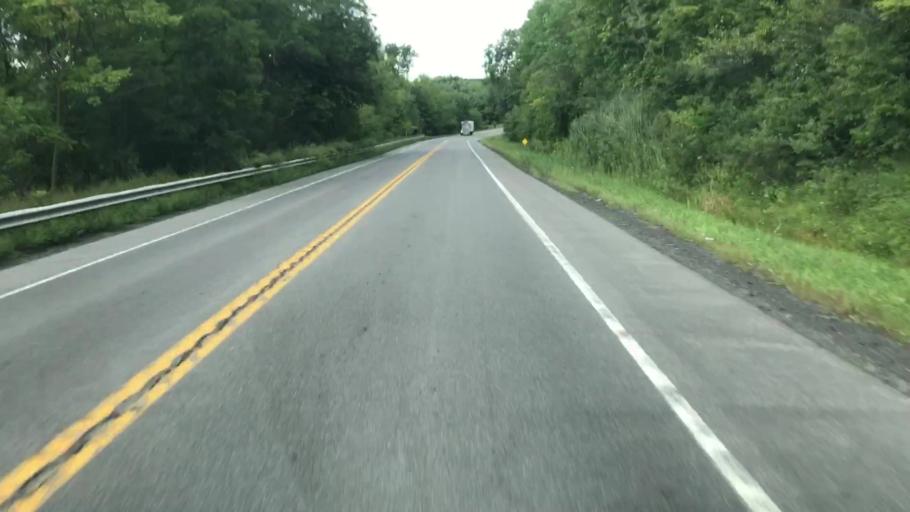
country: US
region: New York
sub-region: Onondaga County
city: Marcellus
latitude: 42.9680
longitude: -76.3367
